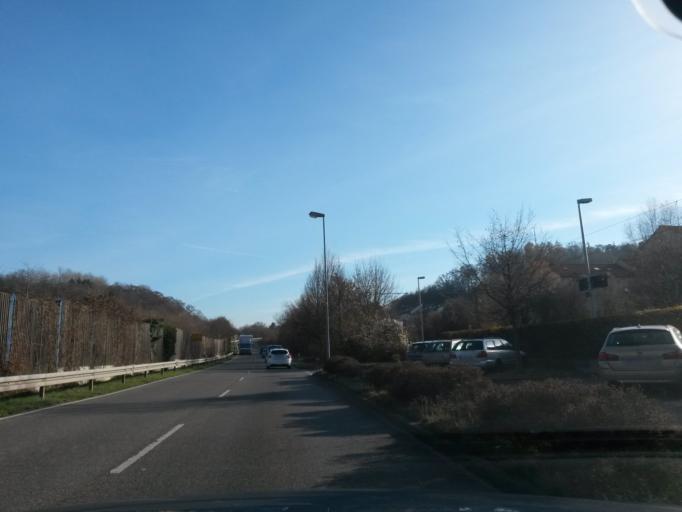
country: DE
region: Baden-Wuerttemberg
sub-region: Karlsruhe Region
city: Ispringen
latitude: 48.9143
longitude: 8.6729
